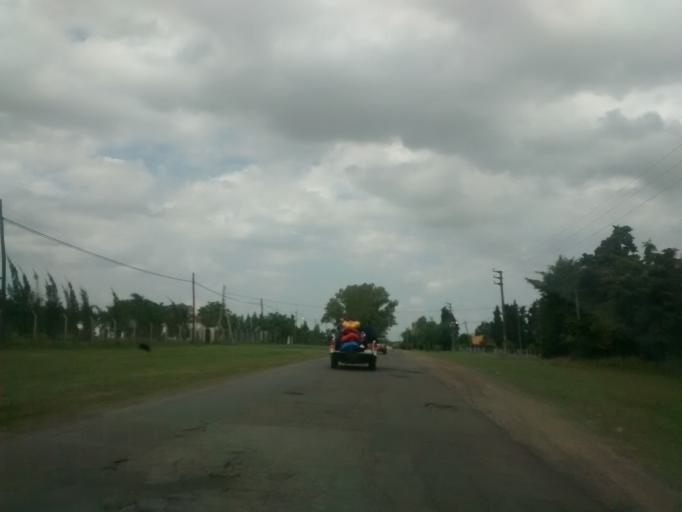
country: AR
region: Buenos Aires
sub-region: Partido de La Plata
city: La Plata
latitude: -34.9964
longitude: -57.9093
